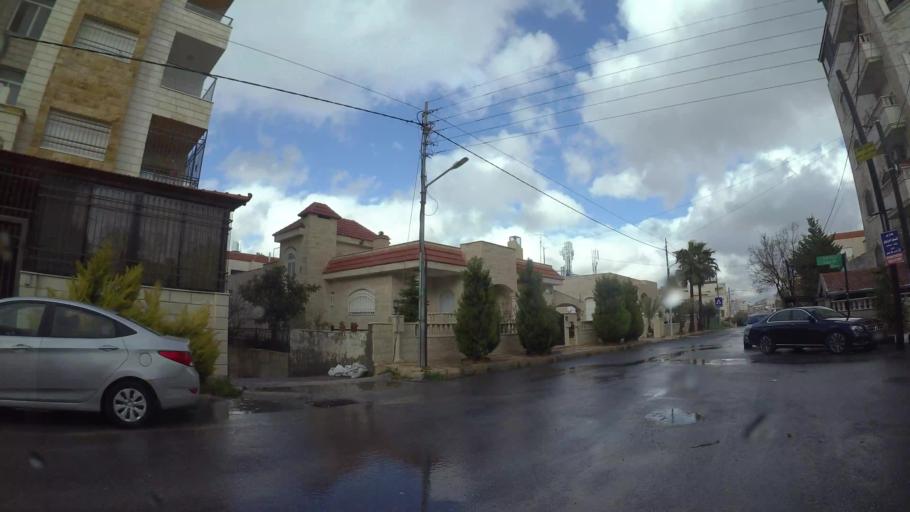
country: JO
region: Amman
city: Al Jubayhah
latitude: 32.0305
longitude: 35.8668
